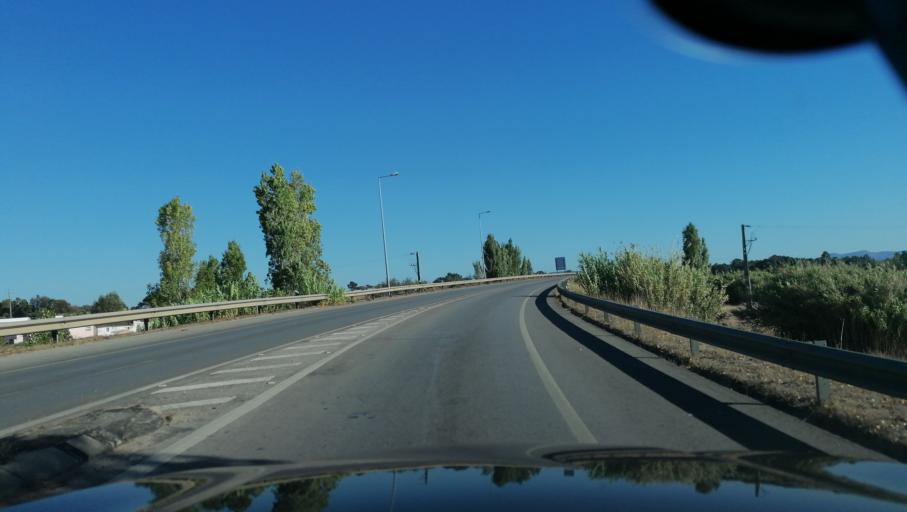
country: PT
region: Setubal
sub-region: Moita
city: Moita
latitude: 38.6423
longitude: -8.9720
